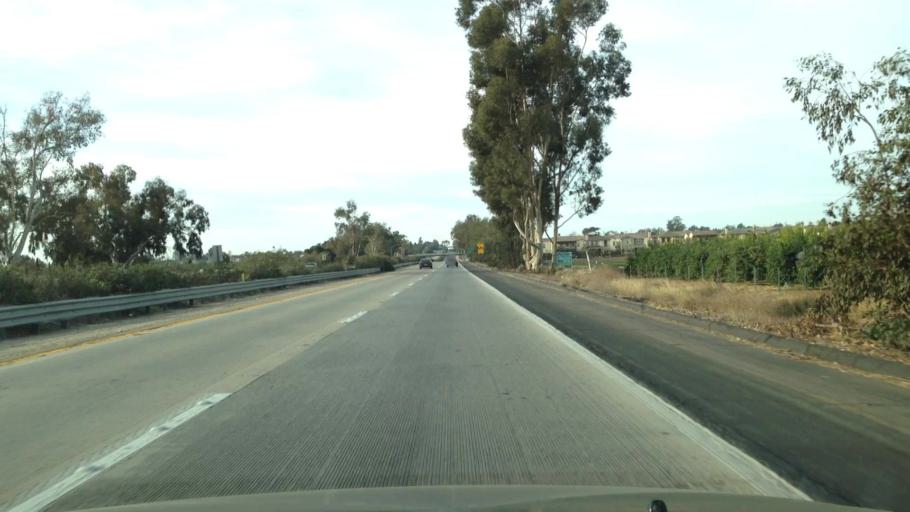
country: US
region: California
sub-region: Ventura County
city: Saticoy
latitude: 34.2955
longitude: -119.1469
